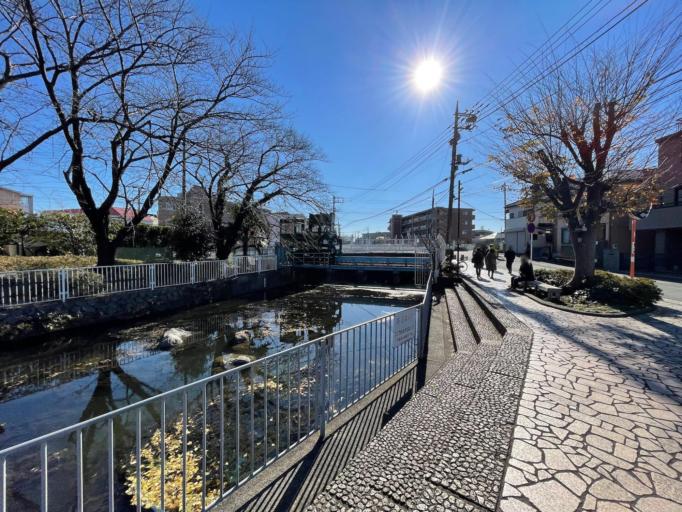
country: JP
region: Tokyo
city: Chofugaoka
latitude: 35.6336
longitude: 139.5438
